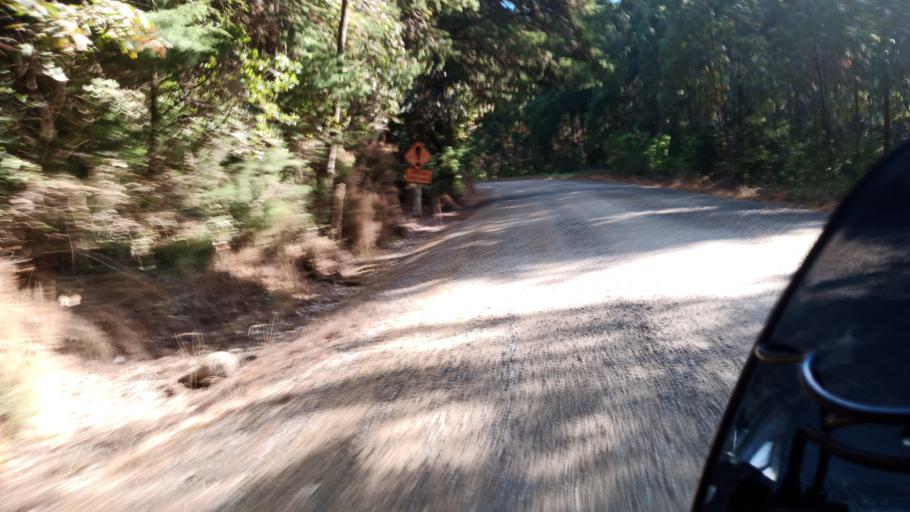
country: NZ
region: Hawke's Bay
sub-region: Wairoa District
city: Wairoa
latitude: -38.9249
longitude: 177.2135
